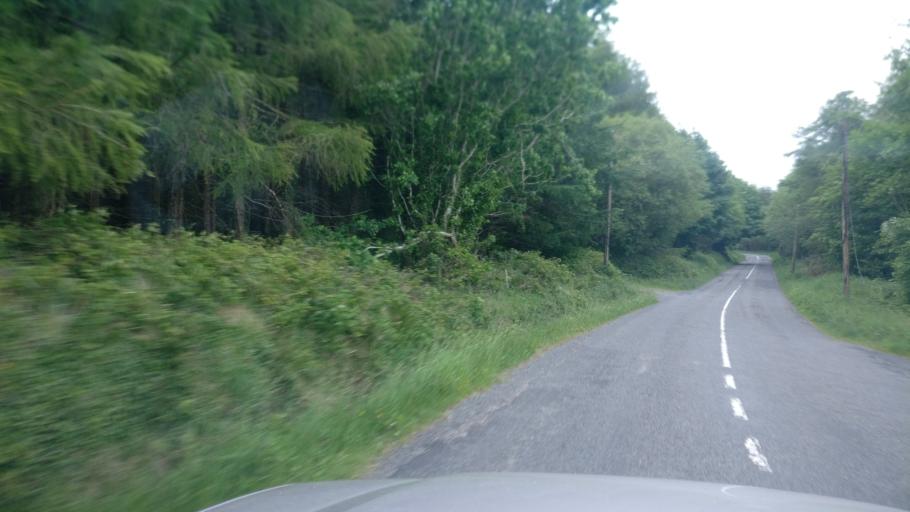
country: IE
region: Connaught
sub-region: County Galway
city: Gort
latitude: 53.0558
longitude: -8.6538
